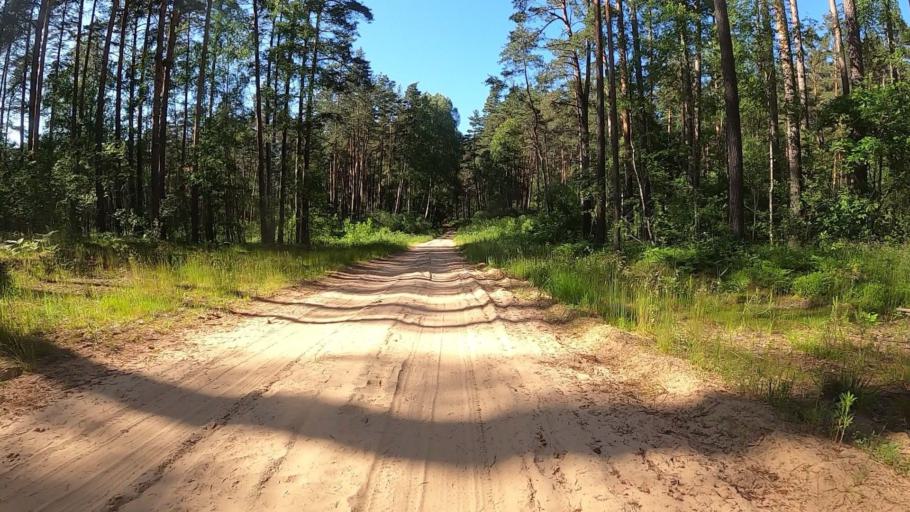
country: LV
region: Riga
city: Bergi
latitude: 57.0367
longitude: 24.2474
